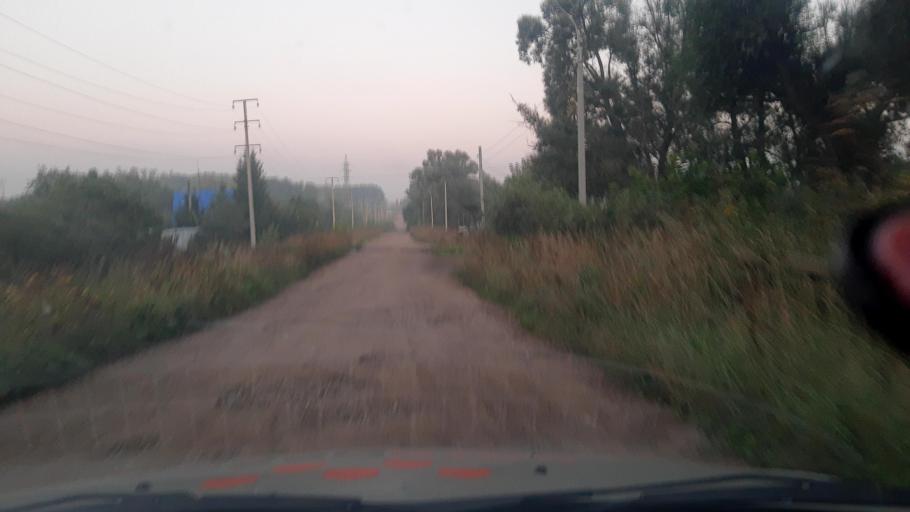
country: RU
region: Bashkortostan
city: Blagoveshchensk
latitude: 55.0505
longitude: 55.9819
